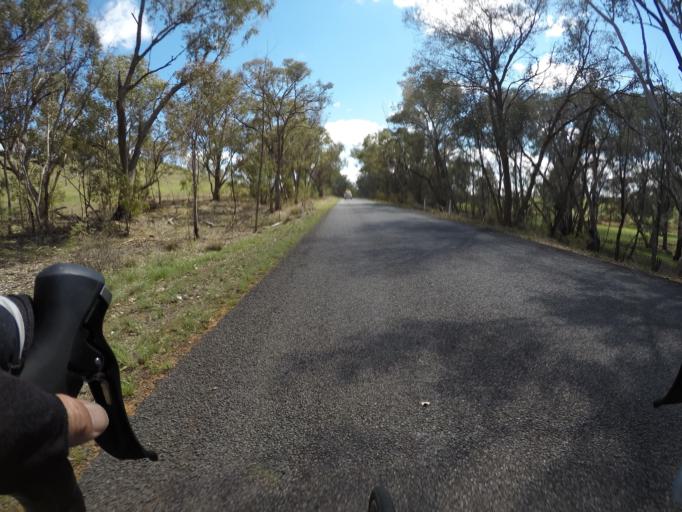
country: AU
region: New South Wales
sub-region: Dubbo Municipality
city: Dubbo
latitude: -32.5402
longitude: 148.5469
